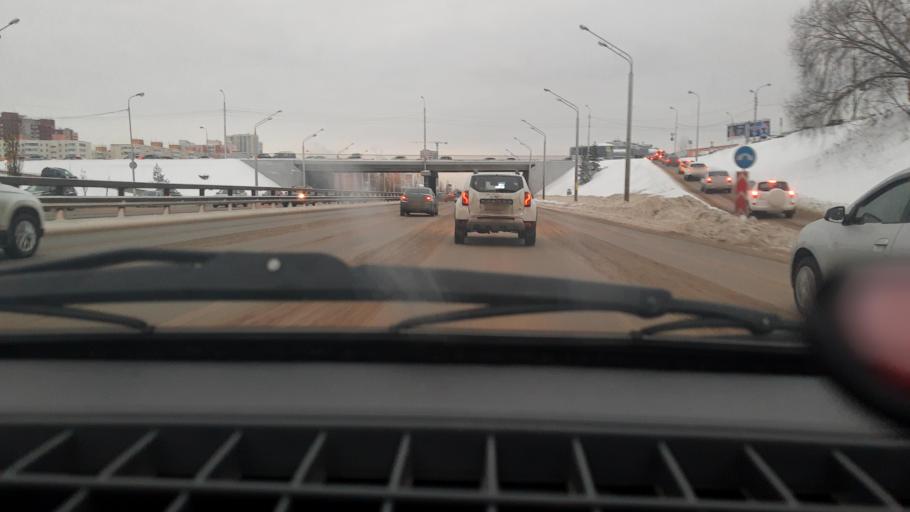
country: RU
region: Bashkortostan
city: Ufa
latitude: 54.7254
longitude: 55.9907
